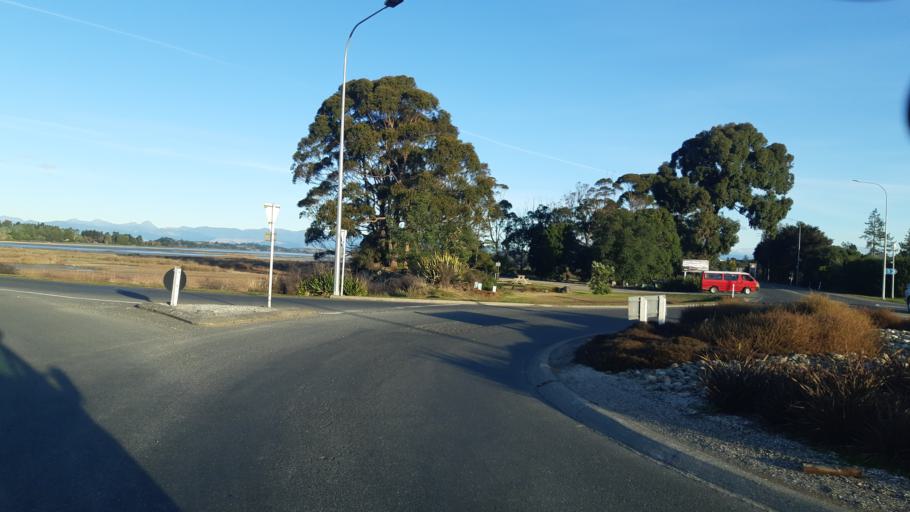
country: NZ
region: Tasman
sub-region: Tasman District
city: Motueka
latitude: -41.1331
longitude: 173.0100
